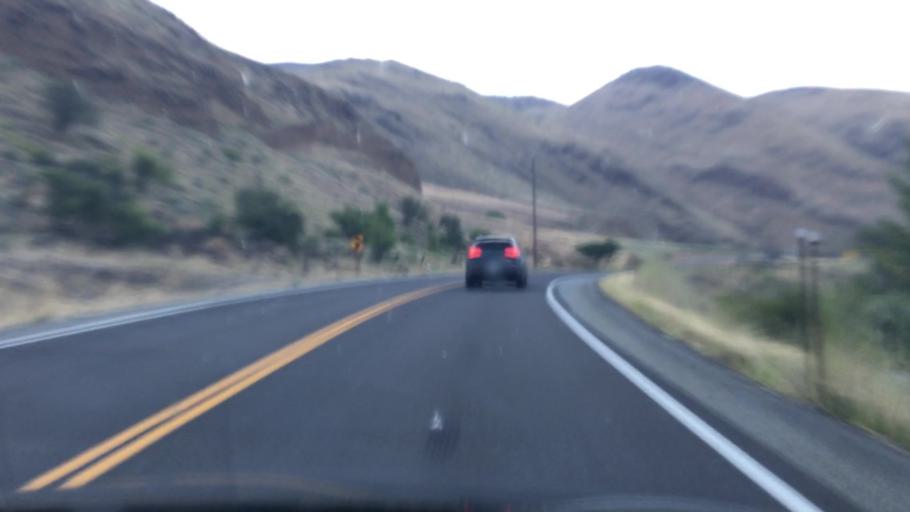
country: US
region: Idaho
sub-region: Valley County
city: McCall
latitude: 45.3894
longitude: -116.3491
